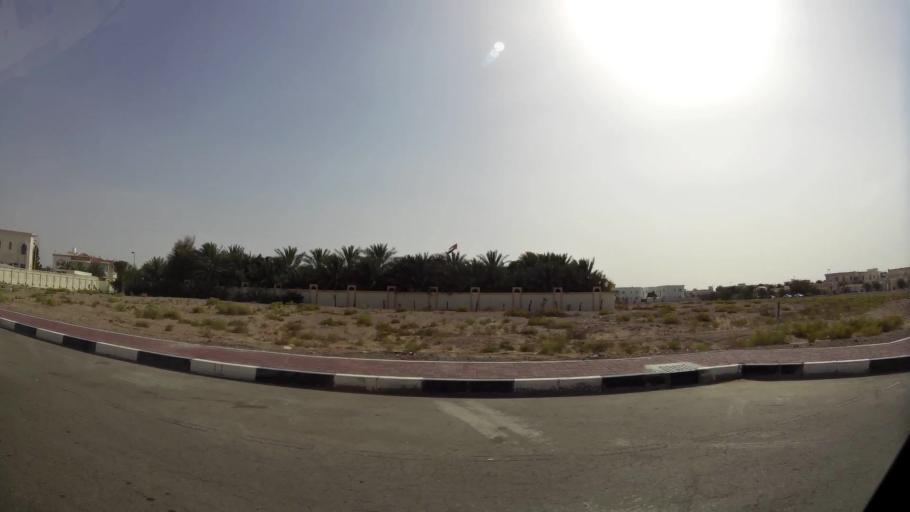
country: AE
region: Abu Dhabi
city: Al Ain
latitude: 24.2344
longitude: 55.6735
